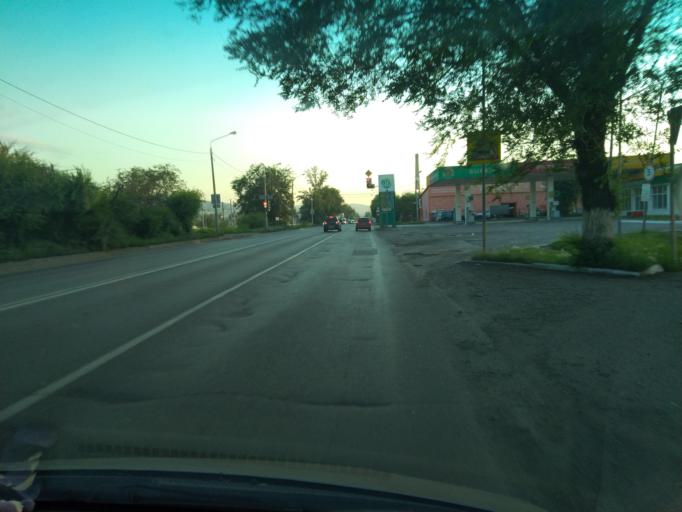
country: RU
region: Krasnoyarskiy
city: Krasnoyarsk
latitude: 55.9932
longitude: 92.9265
